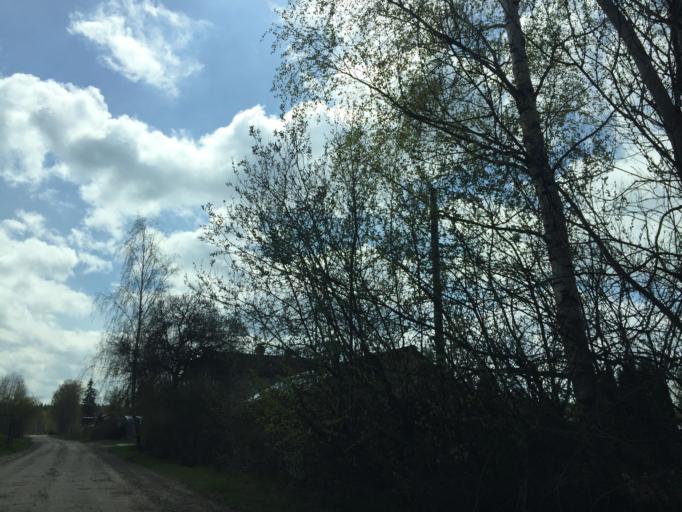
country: LV
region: Kekava
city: Balozi
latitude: 56.8925
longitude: 24.1402
